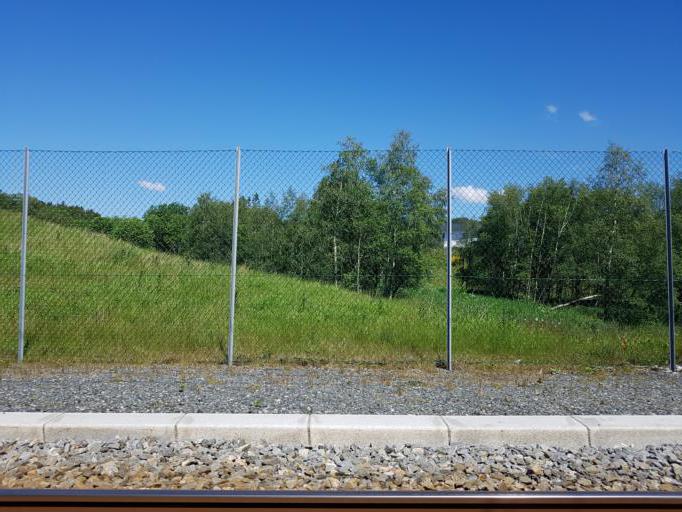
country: NO
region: Hordaland
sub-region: Bergen
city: Ytrebygda
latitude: 60.2922
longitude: 5.2446
